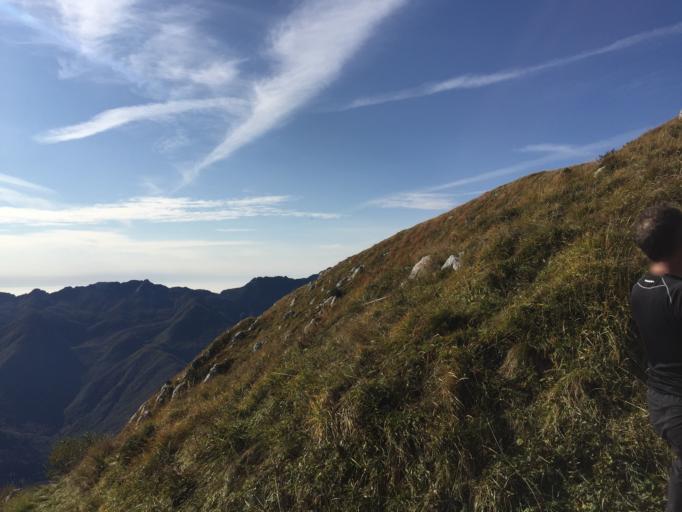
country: IT
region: Friuli Venezia Giulia
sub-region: Provincia di Udine
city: Resiutta
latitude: 46.3471
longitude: 13.2025
